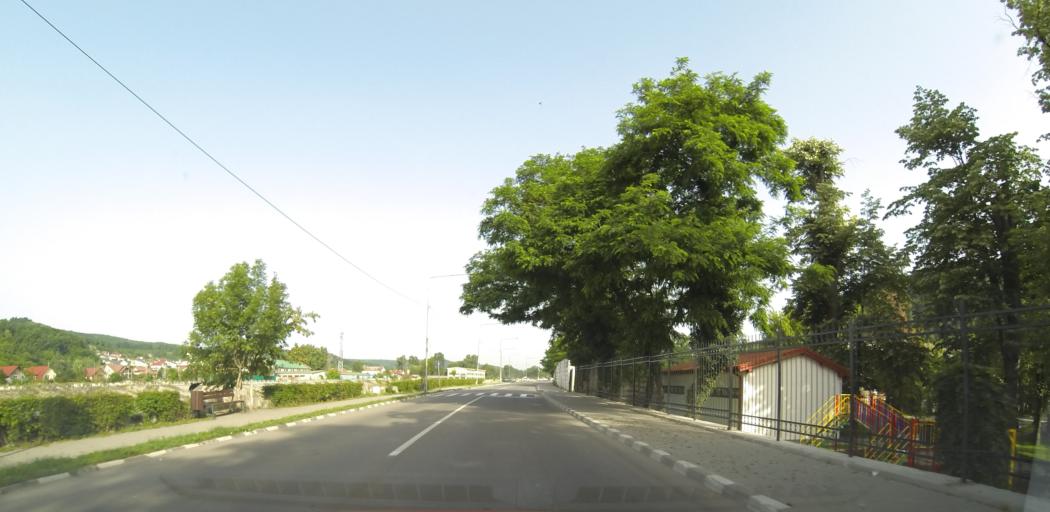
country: RO
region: Valcea
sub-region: Municipiul Ramnicu Valcea
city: Ramnicu Valcea
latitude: 45.1017
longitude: 24.3535
